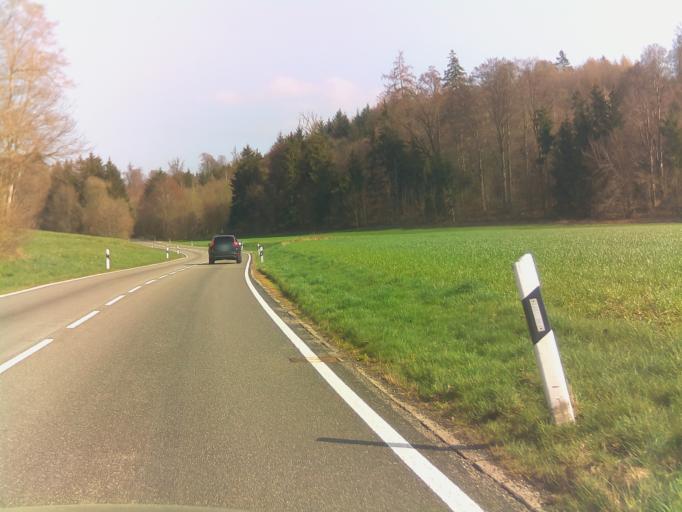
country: DE
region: Bavaria
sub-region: Swabia
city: Unterroth
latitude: 48.1958
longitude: 10.1835
